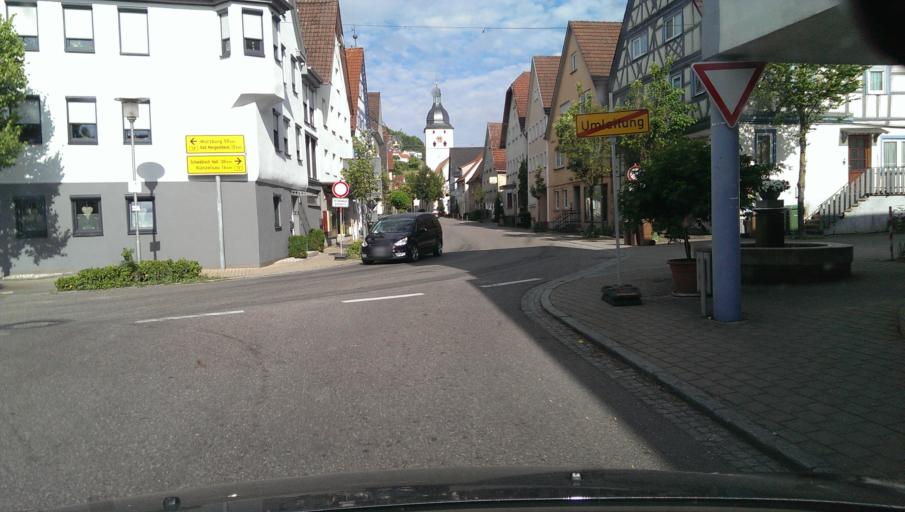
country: DE
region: Baden-Wuerttemberg
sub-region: Regierungsbezirk Stuttgart
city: Dorzbach
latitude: 49.3836
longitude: 9.7056
